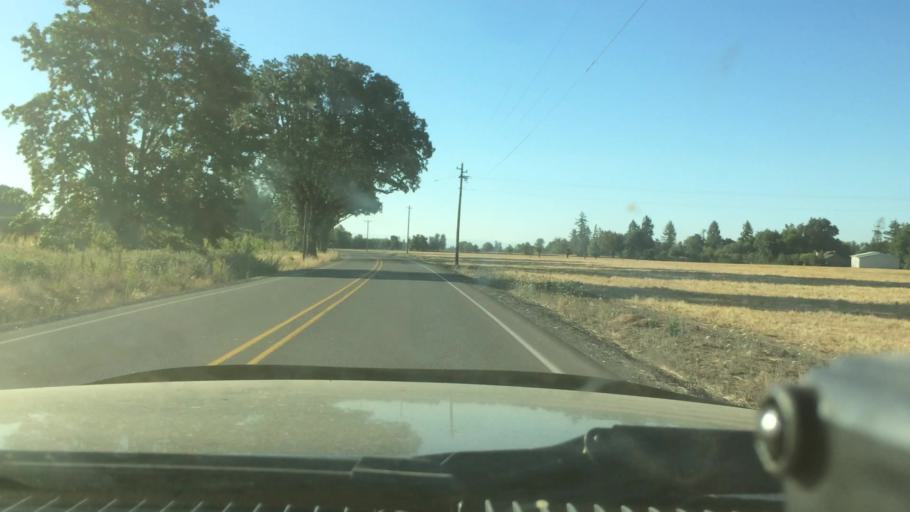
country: US
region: Oregon
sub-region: Marion County
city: Gervais
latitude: 45.1309
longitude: -123.0023
